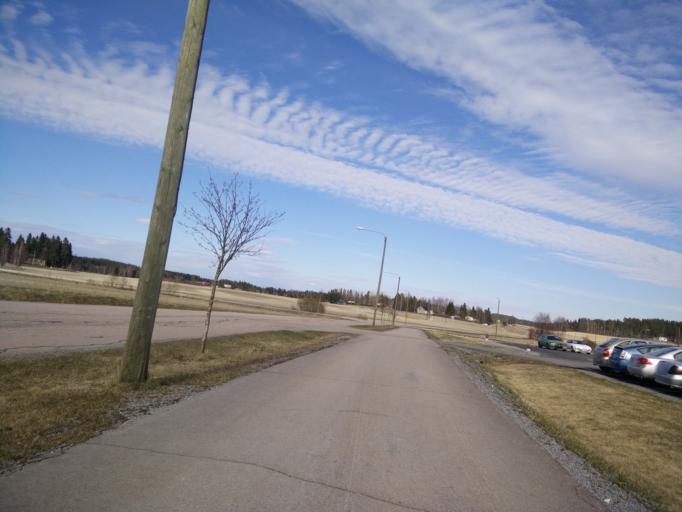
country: FI
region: Pirkanmaa
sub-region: Tampere
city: Orivesi
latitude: 61.6872
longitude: 24.3722
